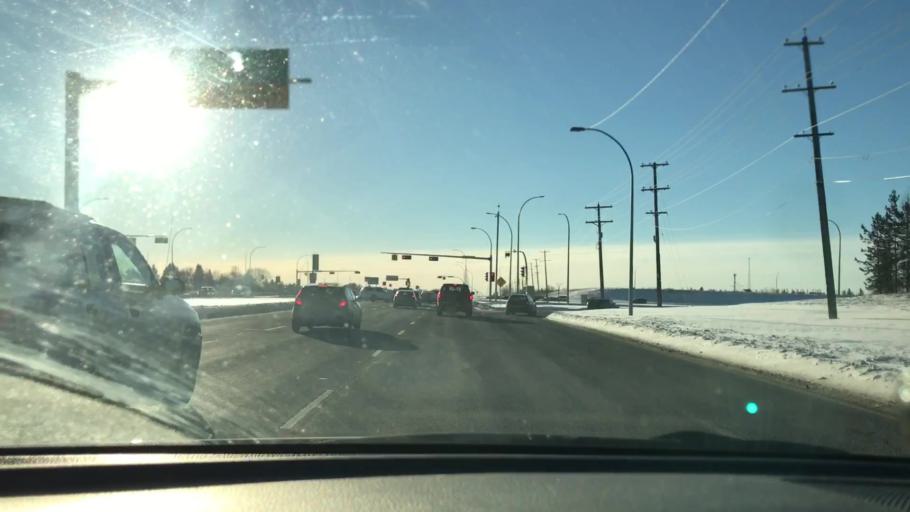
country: CA
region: Alberta
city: Edmonton
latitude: 53.4844
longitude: -113.4672
